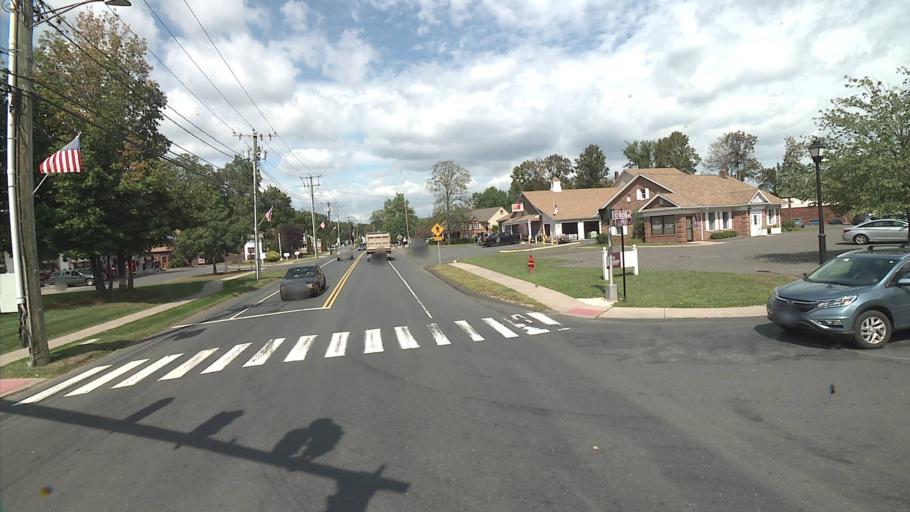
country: US
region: Connecticut
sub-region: Hartford County
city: Salmon Brook
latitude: 41.9511
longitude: -72.7861
